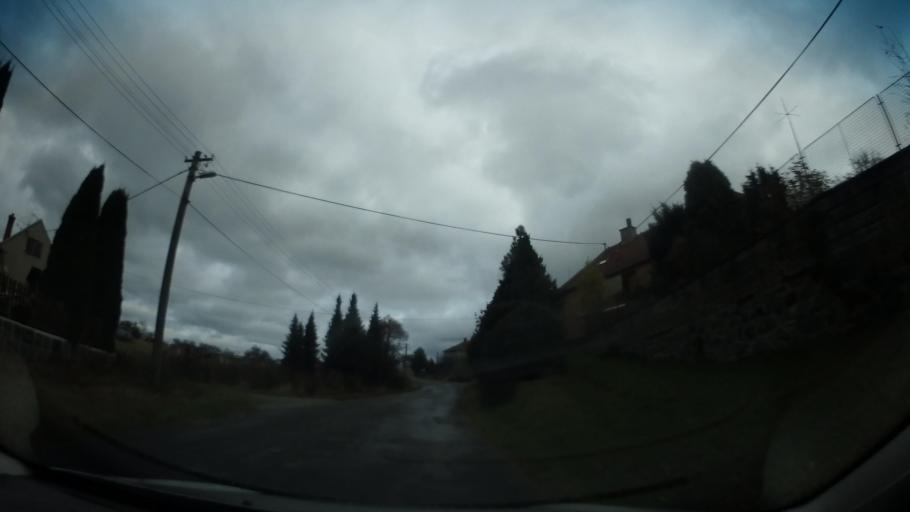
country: CZ
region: Vysocina
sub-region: Okres Zd'ar nad Sazavou
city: Velka Bites
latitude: 49.2909
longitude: 16.1431
